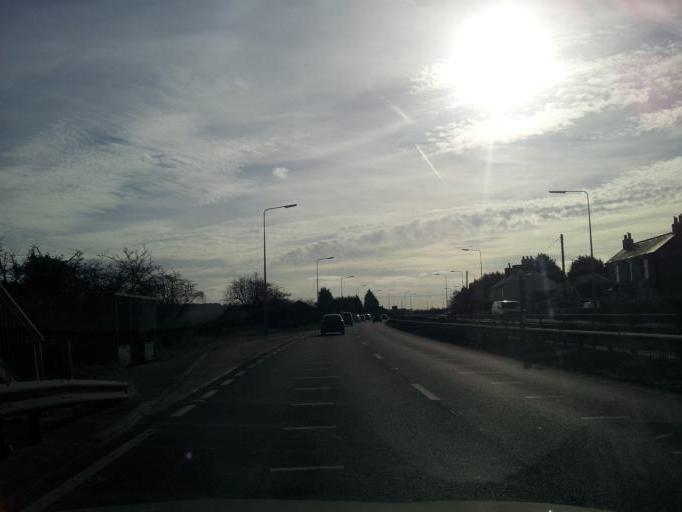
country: GB
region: England
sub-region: Central Bedfordshire
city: Sandy
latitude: 52.1209
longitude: -0.2927
